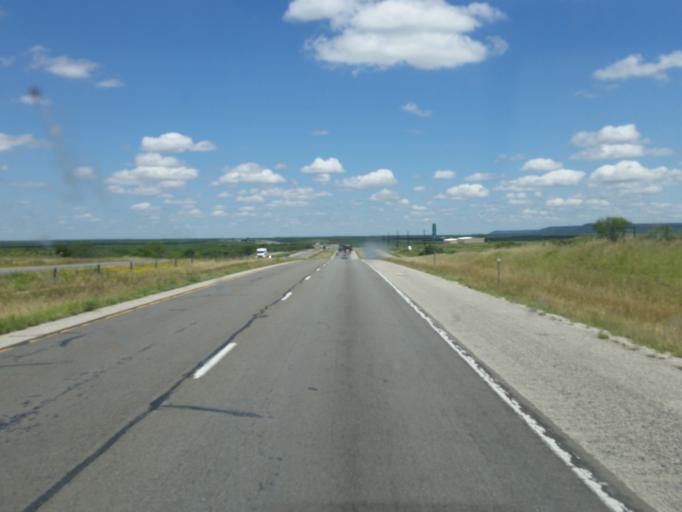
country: US
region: Texas
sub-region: Nolan County
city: Sweetwater
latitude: 32.4953
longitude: -100.2639
